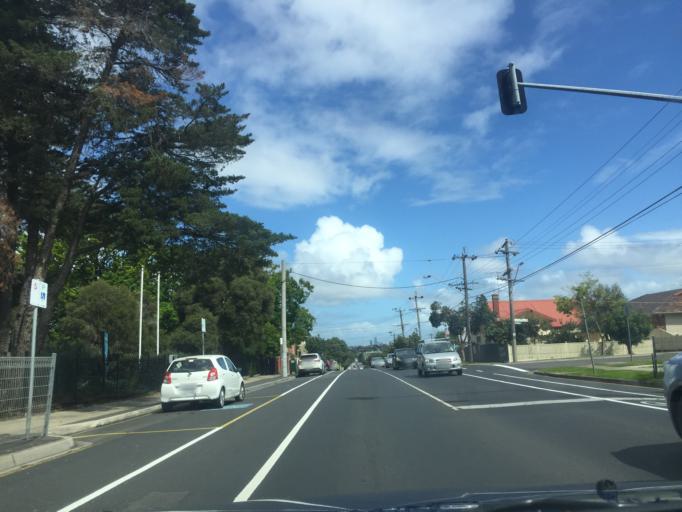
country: AU
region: Victoria
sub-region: Darebin
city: Preston
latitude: -37.7544
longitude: 145.0140
